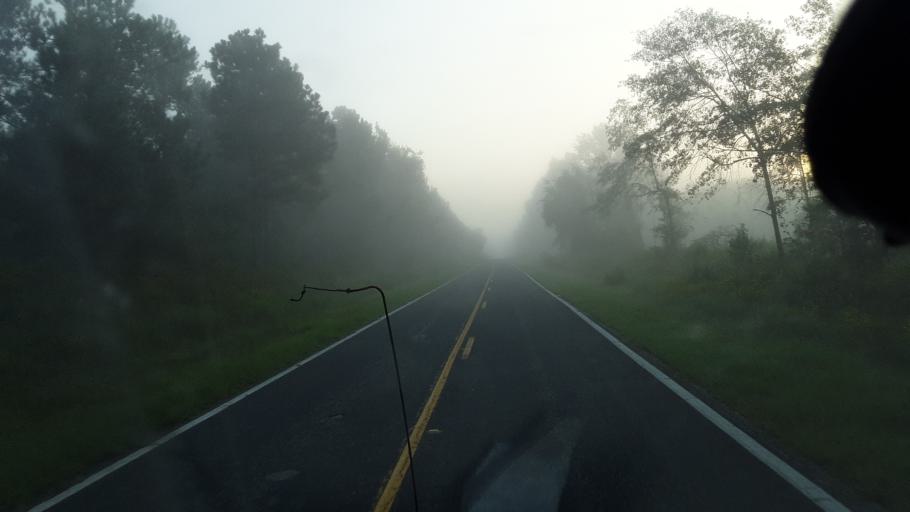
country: US
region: South Carolina
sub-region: Clarendon County
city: Manning
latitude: 33.7624
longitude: -80.0492
